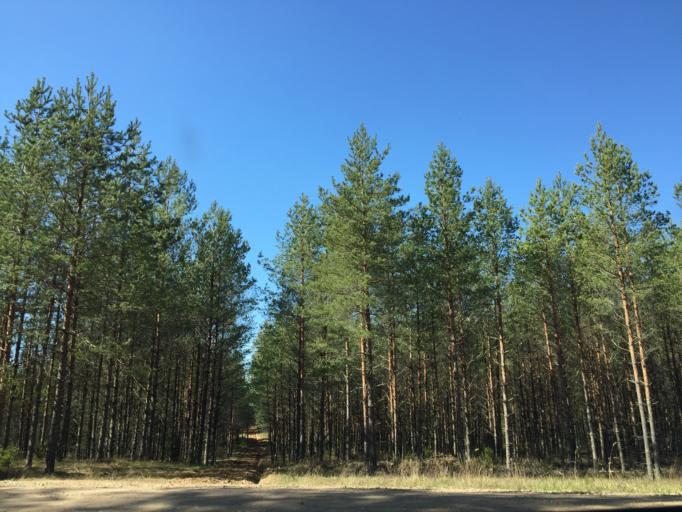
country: LV
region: Strenci
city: Strenci
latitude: 57.5973
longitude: 25.7059
